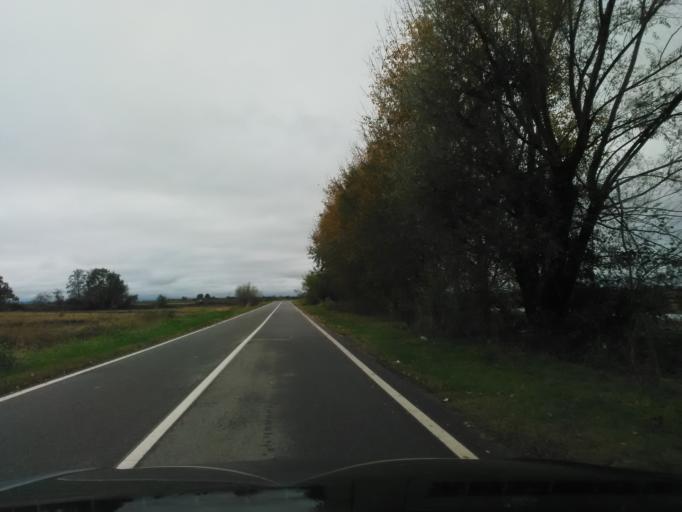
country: IT
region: Piedmont
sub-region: Provincia di Vercelli
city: Olcenengo
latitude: 45.3589
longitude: 8.3070
